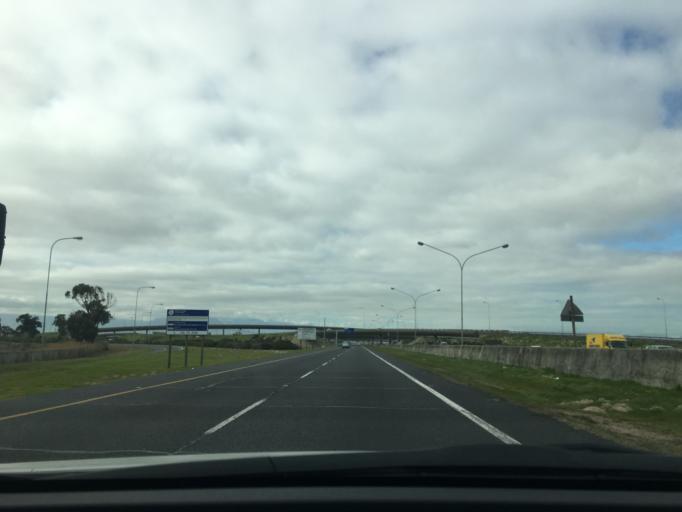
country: ZA
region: Western Cape
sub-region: City of Cape Town
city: Lansdowne
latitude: -33.9988
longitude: 18.6268
